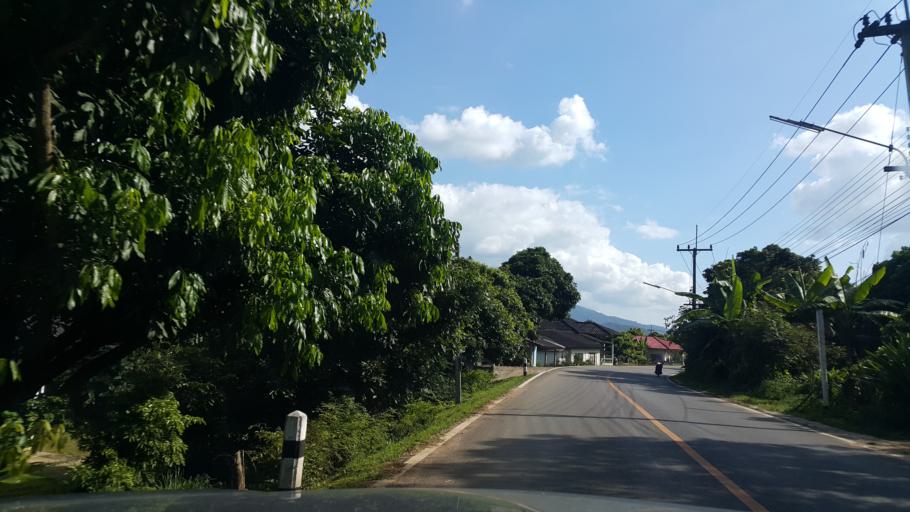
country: TH
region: Lamphun
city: Ban Thi
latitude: 18.5682
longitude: 99.2566
